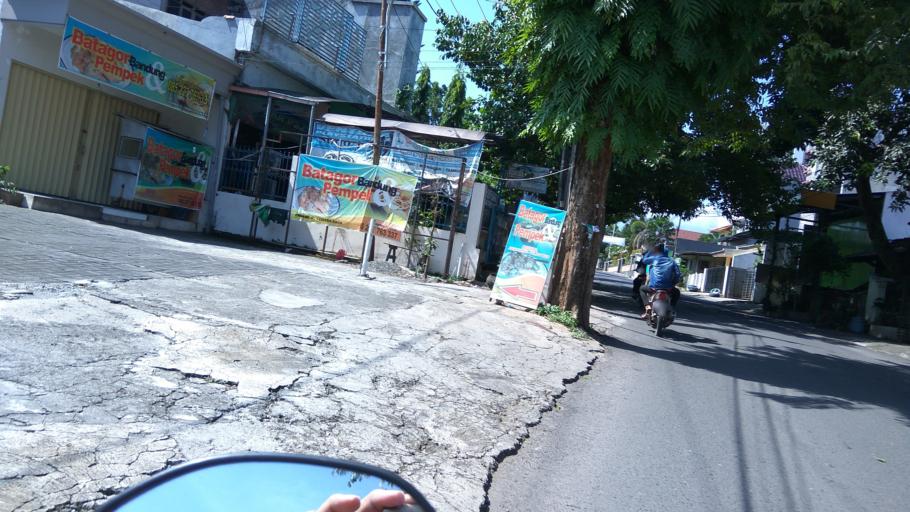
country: ID
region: Central Java
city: Ungaran
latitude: -7.0719
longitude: 110.4231
